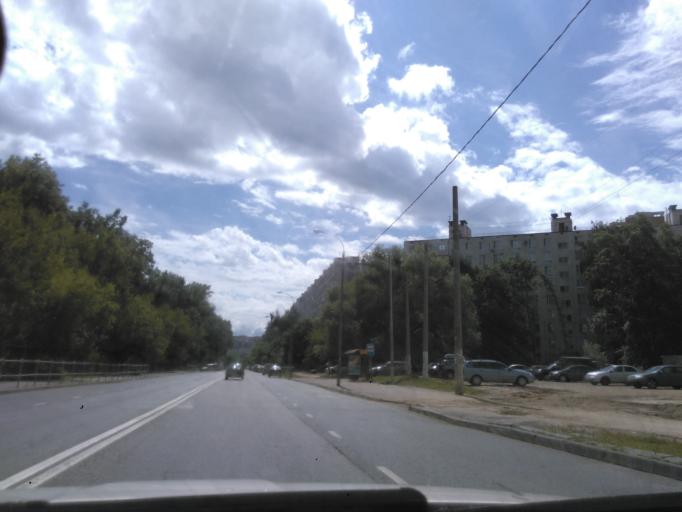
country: RU
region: Moscow
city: Novokhovrino
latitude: 55.8666
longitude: 37.5017
